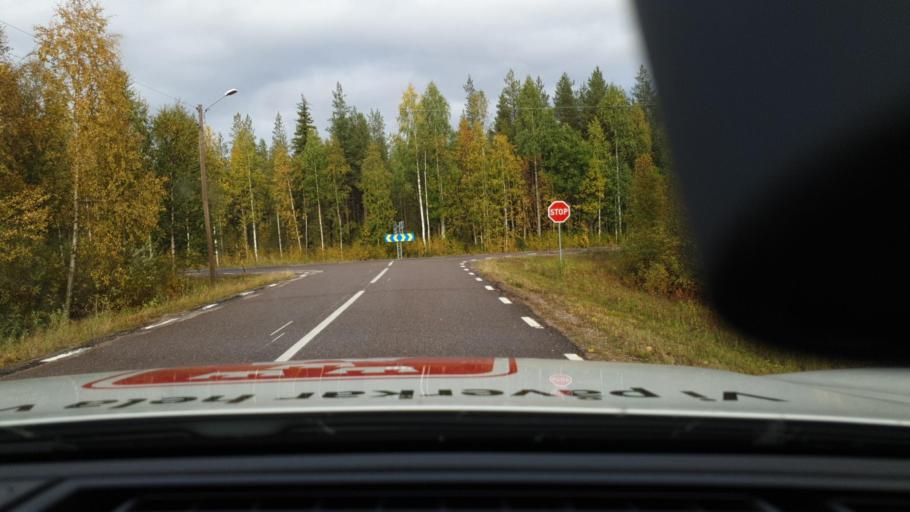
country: SE
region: Norrbotten
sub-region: Overkalix Kommun
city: OEverkalix
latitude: 67.0096
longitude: 22.5343
